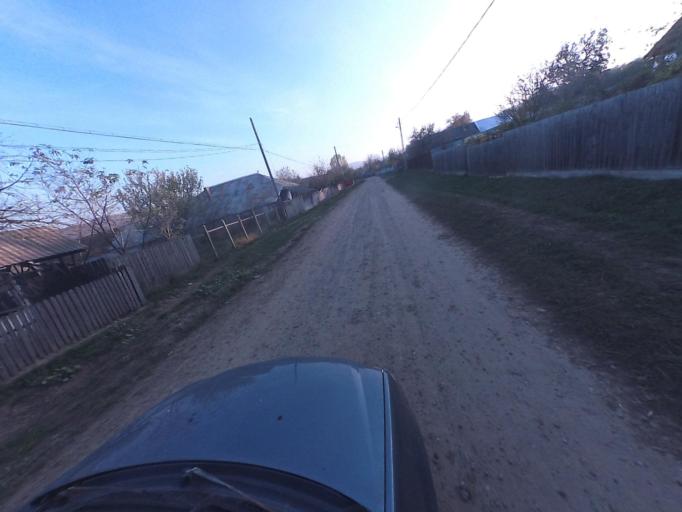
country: RO
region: Vaslui
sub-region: Comuna Bacesti
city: Bacesti
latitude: 46.8059
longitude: 27.2246
